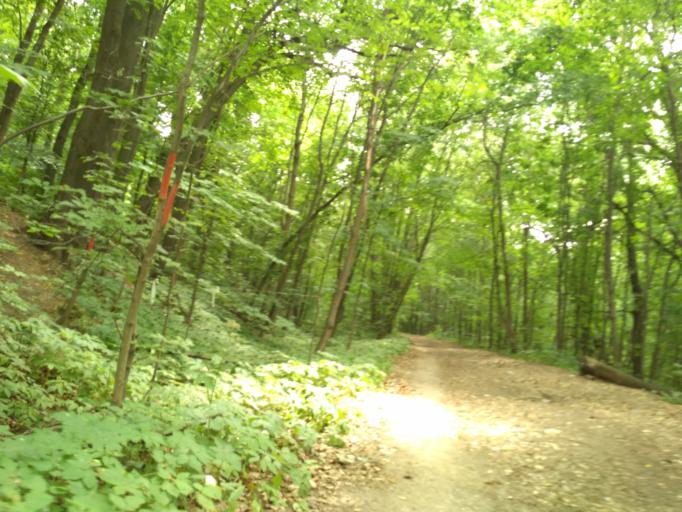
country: RU
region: Nizjnij Novgorod
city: Nizhniy Novgorod
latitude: 56.2624
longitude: 43.9712
